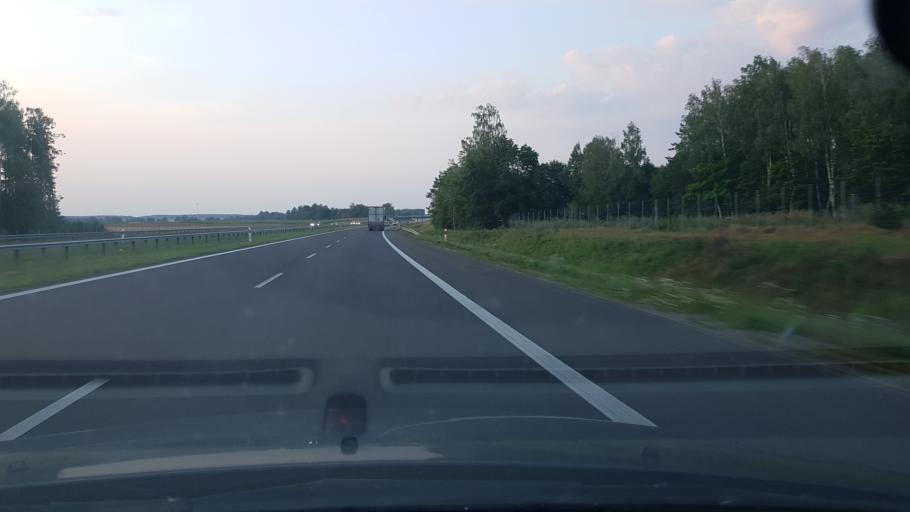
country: PL
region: Masovian Voivodeship
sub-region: Powiat mlawski
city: Wieczfnia Koscielna
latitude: 53.2569
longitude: 20.4253
